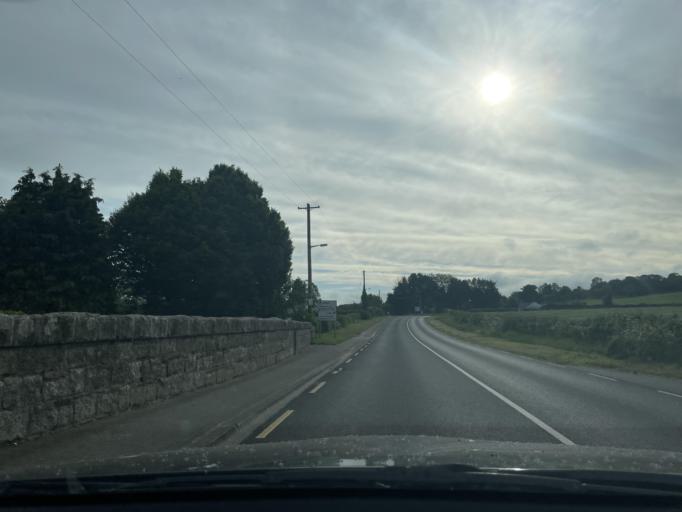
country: IE
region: Leinster
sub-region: County Carlow
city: Bagenalstown
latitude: 52.6326
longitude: -6.9810
